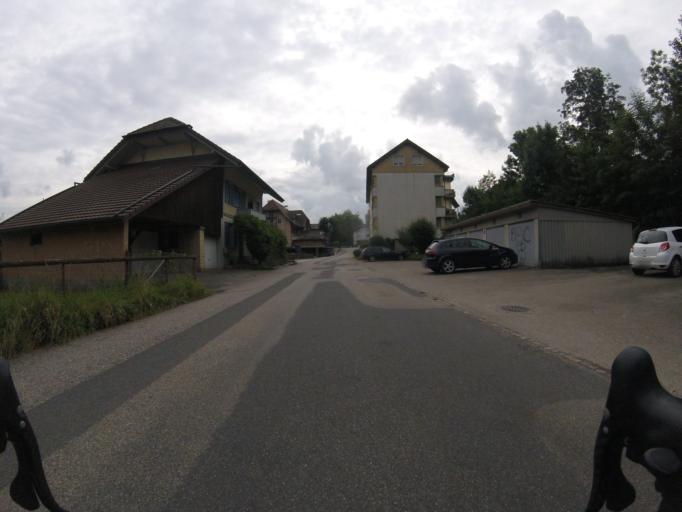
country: CH
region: Bern
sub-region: Emmental District
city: Oberburg
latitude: 47.0178
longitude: 7.6562
